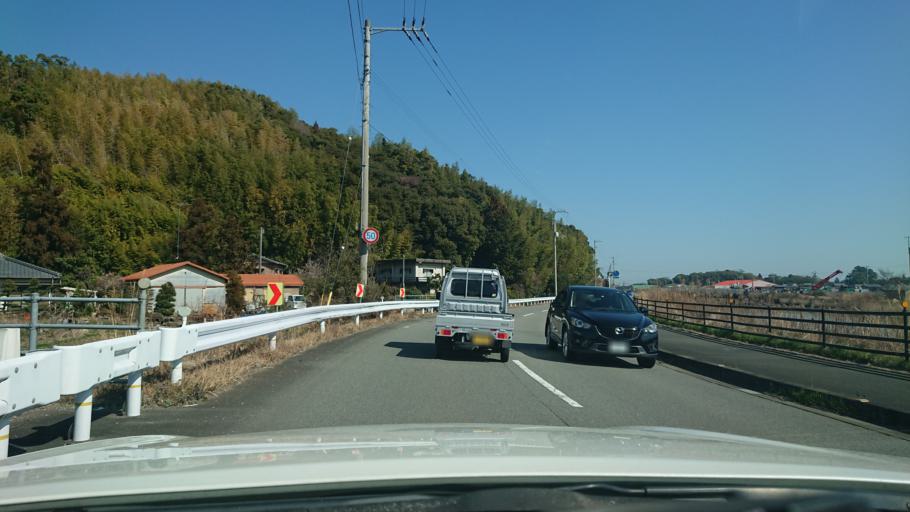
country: JP
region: Tokushima
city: Komatsushimacho
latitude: 33.9718
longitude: 134.5999
